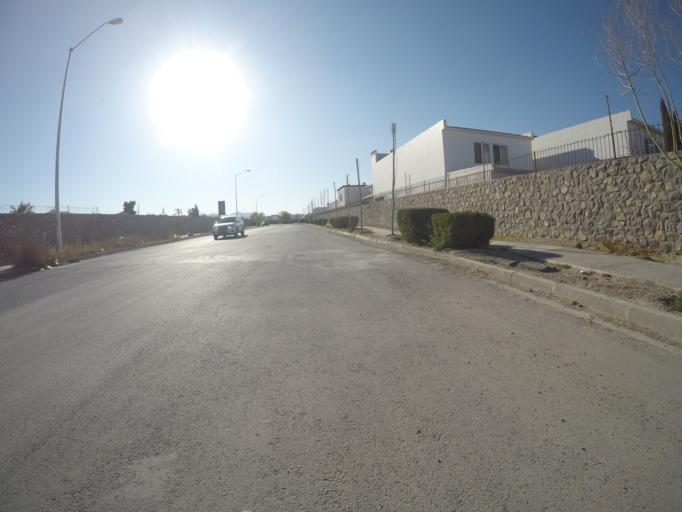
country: MX
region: Chihuahua
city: Ciudad Juarez
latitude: 31.7030
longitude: -106.3929
